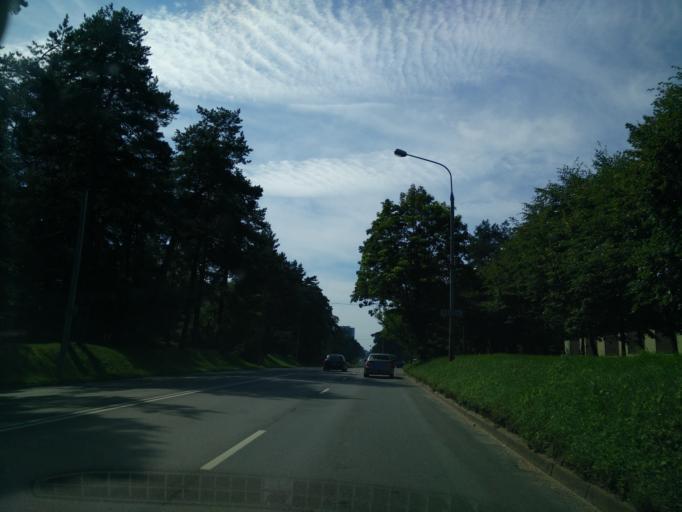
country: LT
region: Vilnius County
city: Rasos
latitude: 54.7315
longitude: 25.3331
